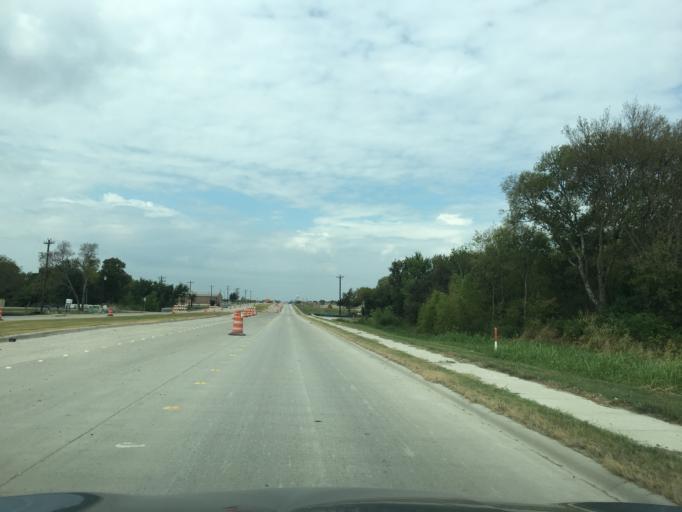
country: US
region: Texas
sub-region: Collin County
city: Melissa
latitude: 33.2975
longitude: -96.5378
